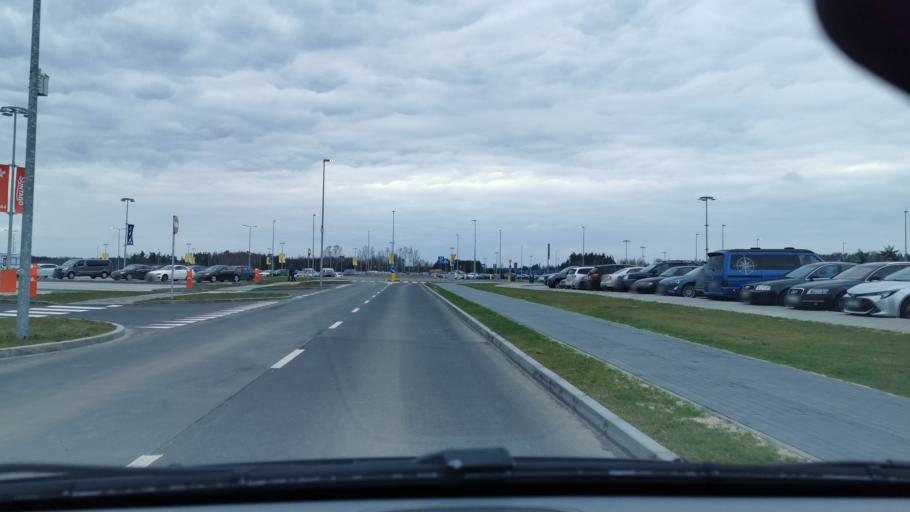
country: PL
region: Masovian Voivodeship
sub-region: Powiat zyrardowski
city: Mszczonow
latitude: 51.9885
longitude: 20.4616
